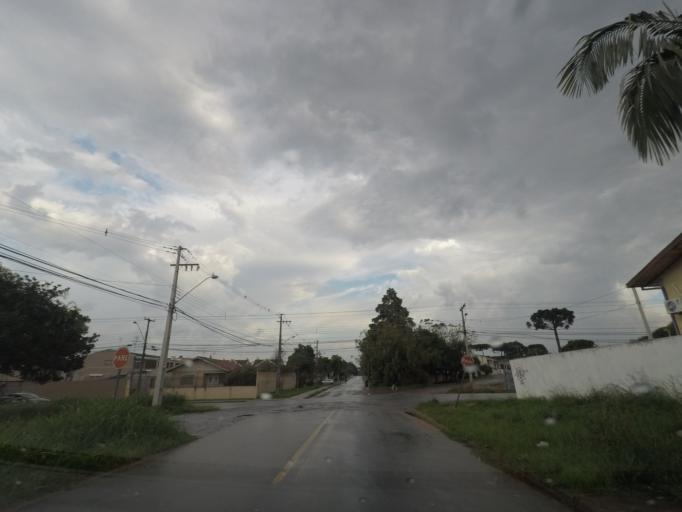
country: BR
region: Parana
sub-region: Sao Jose Dos Pinhais
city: Sao Jose dos Pinhais
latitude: -25.4936
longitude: -49.2468
